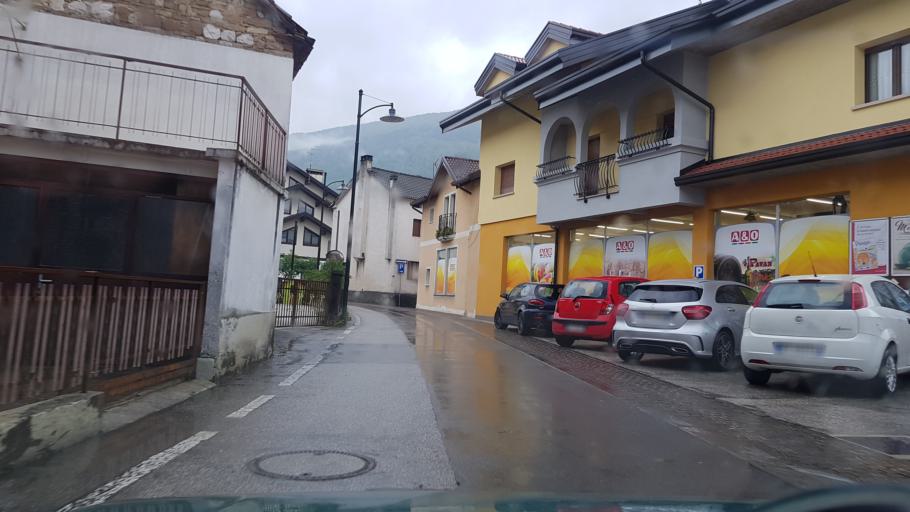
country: IT
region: Veneto
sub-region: Provincia di Belluno
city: Farra d'Alpago
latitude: 46.1214
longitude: 12.3577
